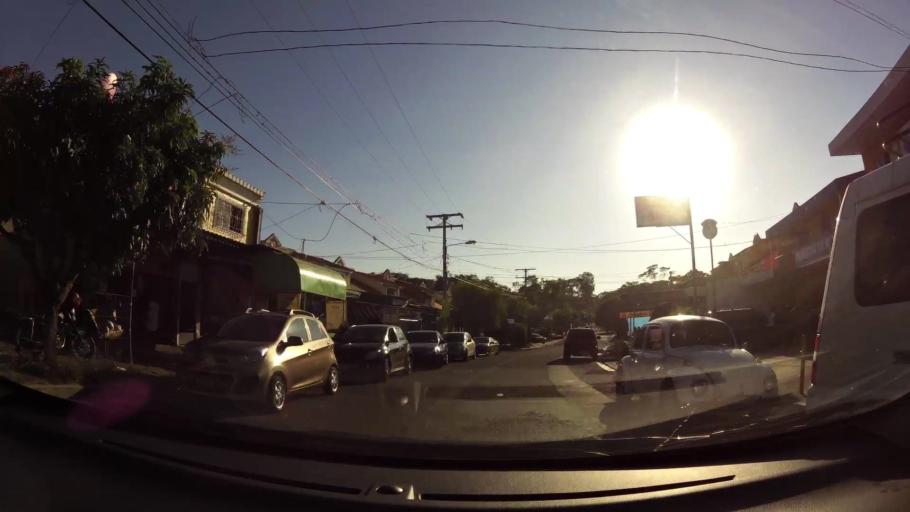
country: SV
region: La Libertad
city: Santa Tecla
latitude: 13.7392
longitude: -89.3574
